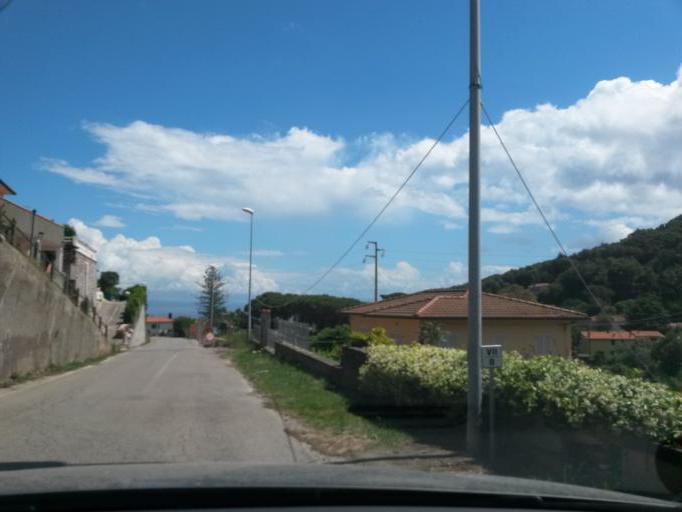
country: IT
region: Tuscany
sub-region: Provincia di Livorno
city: Rio Marina
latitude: 42.8576
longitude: 10.4152
